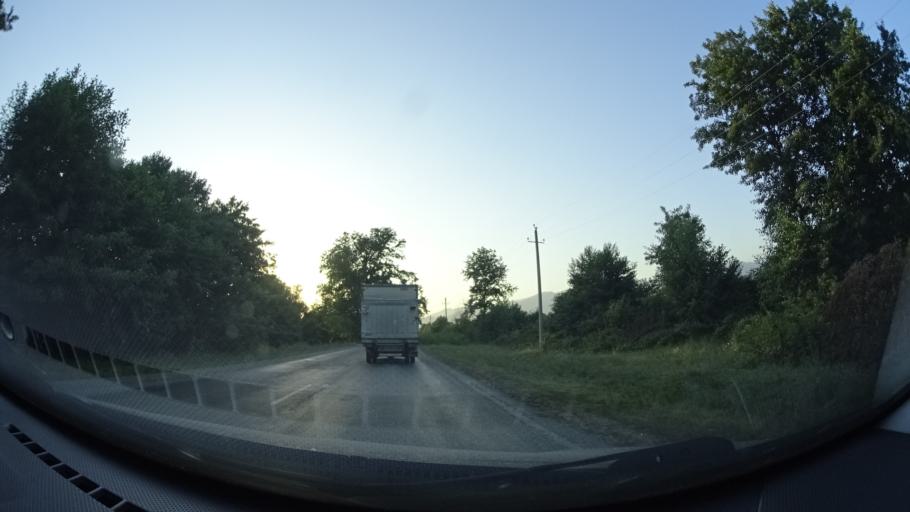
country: GE
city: Bagdadi
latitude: 41.8587
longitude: 46.0256
